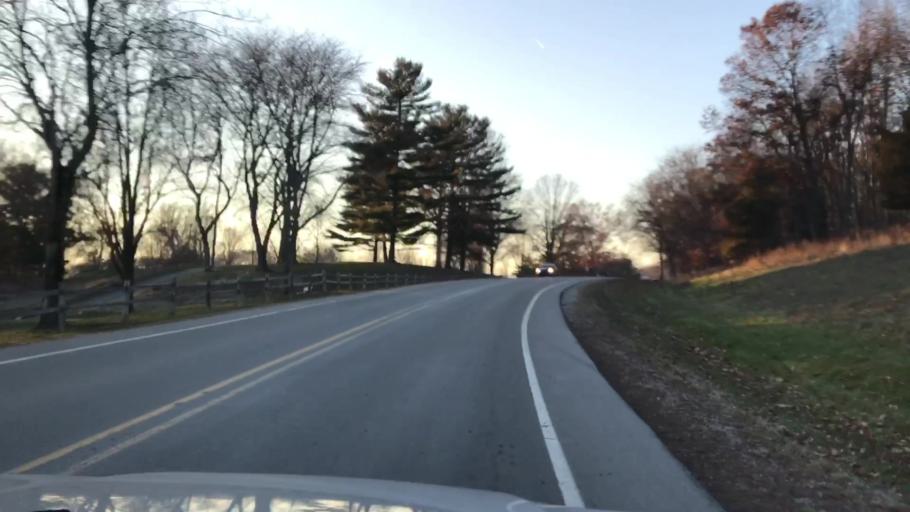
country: US
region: Michigan
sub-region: Oakland County
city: South Lyon
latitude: 42.5223
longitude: -83.6803
